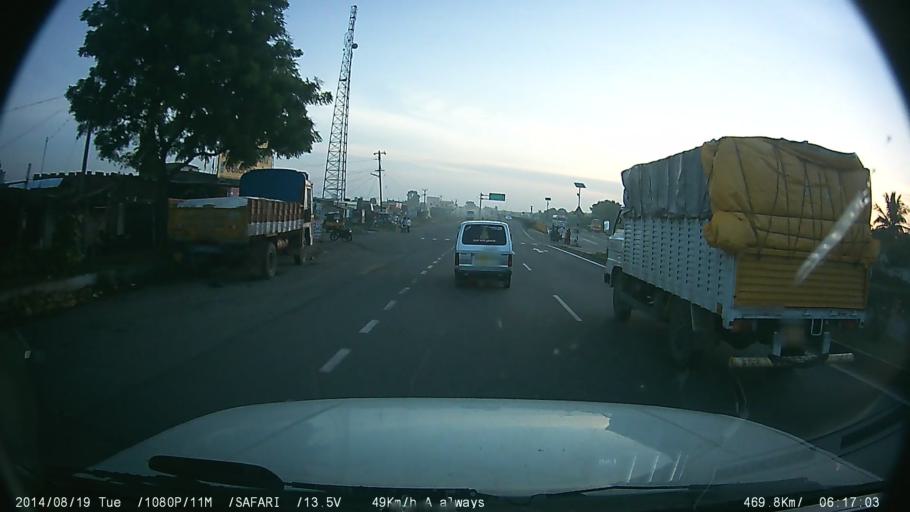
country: IN
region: Tamil Nadu
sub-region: Dharmapuri
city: Dharmapuri
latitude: 11.9920
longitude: 78.0672
